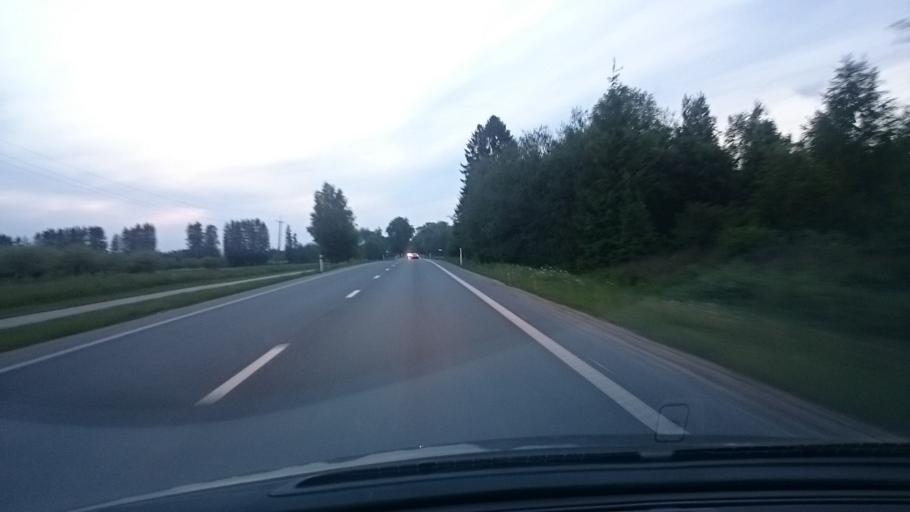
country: EE
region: Raplamaa
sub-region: Kehtna vald
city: Kehtna
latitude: 58.9733
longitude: 24.8501
